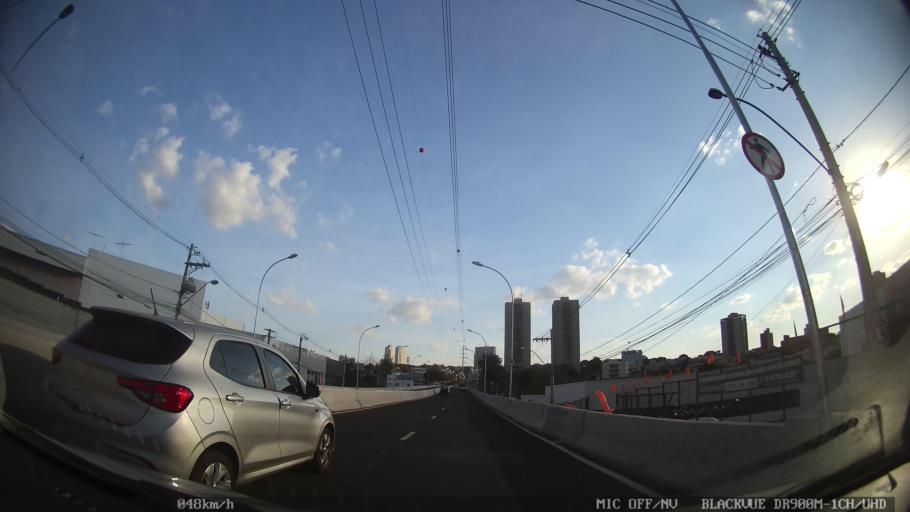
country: BR
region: Sao Paulo
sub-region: Ribeirao Preto
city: Ribeirao Preto
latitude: -21.1914
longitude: -47.7965
